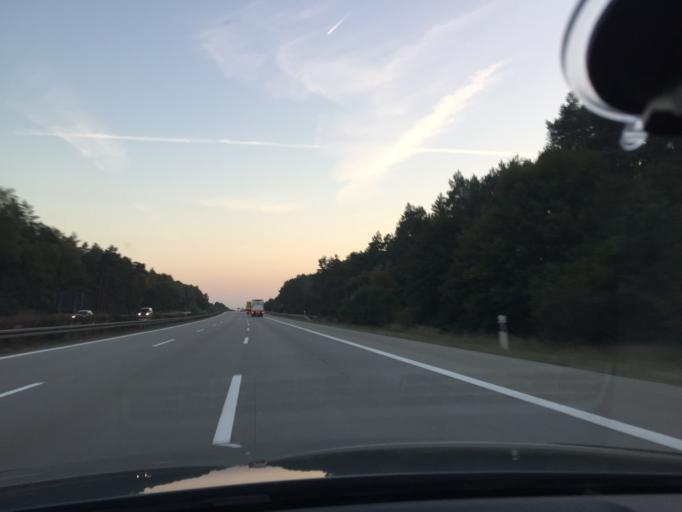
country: DE
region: Brandenburg
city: Erkner
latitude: 52.3629
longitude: 13.7613
